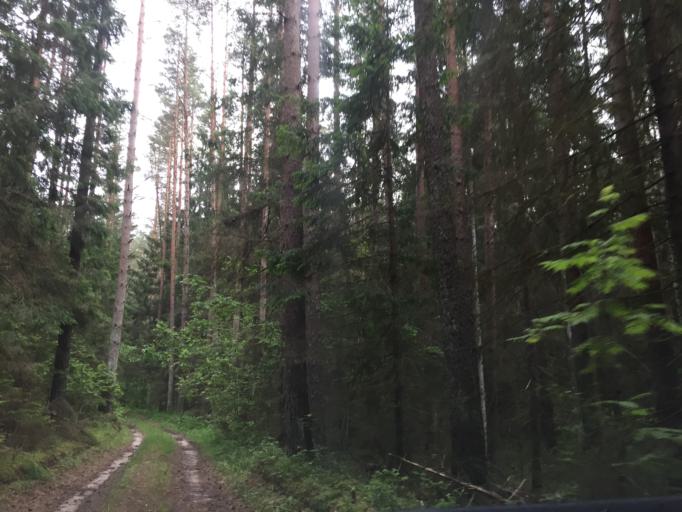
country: LV
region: Tukuma Rajons
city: Tukums
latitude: 57.0236
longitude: 23.0764
